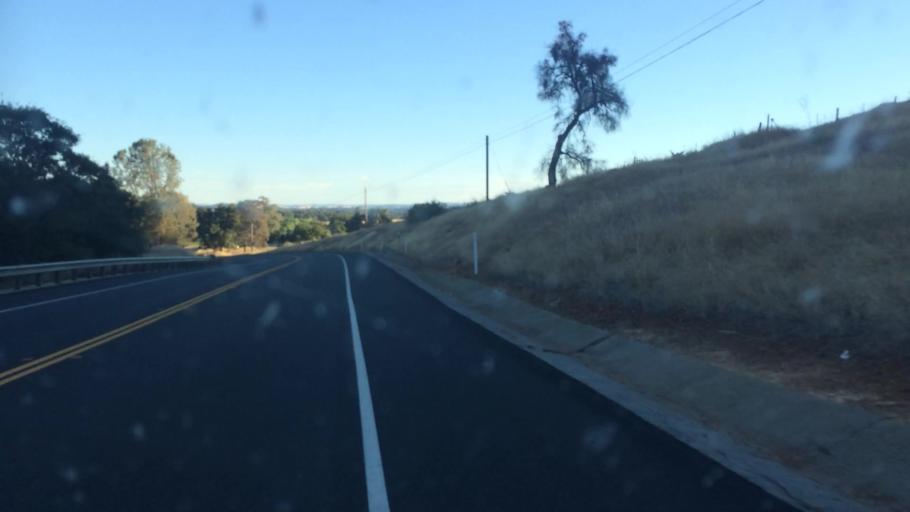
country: US
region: California
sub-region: El Dorado County
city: Deer Park
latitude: 38.6488
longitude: -120.8511
